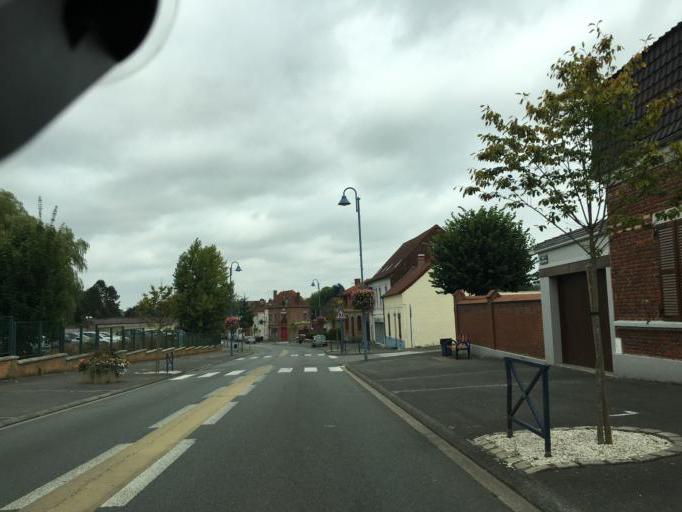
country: FR
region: Nord-Pas-de-Calais
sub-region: Departement du Pas-de-Calais
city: Saint-Pol-sur-Ternoise
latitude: 50.3758
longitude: 2.3332
